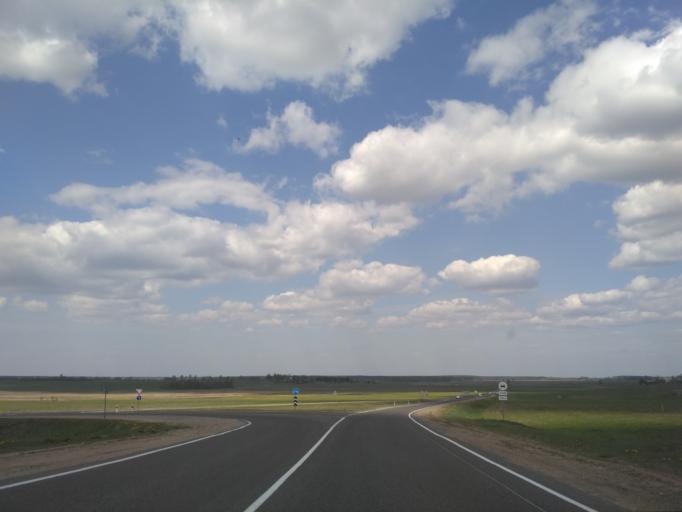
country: BY
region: Minsk
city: Vilyeyka
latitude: 54.5264
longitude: 26.8698
